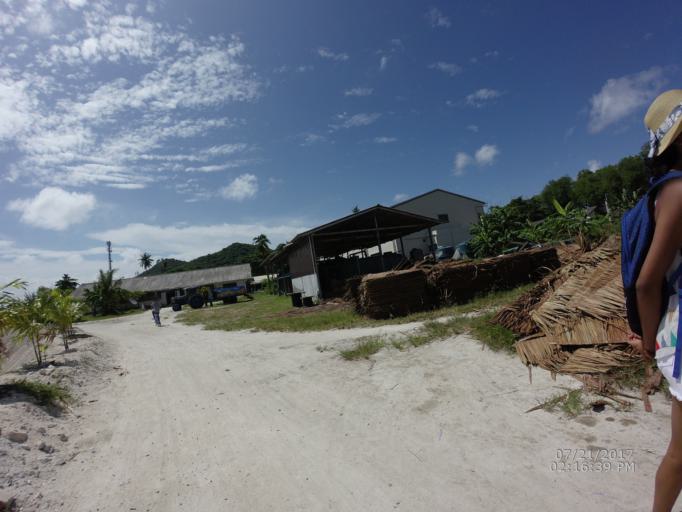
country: TH
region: Phangnga
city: Ban Phru Nai
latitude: 7.7592
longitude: 98.7706
